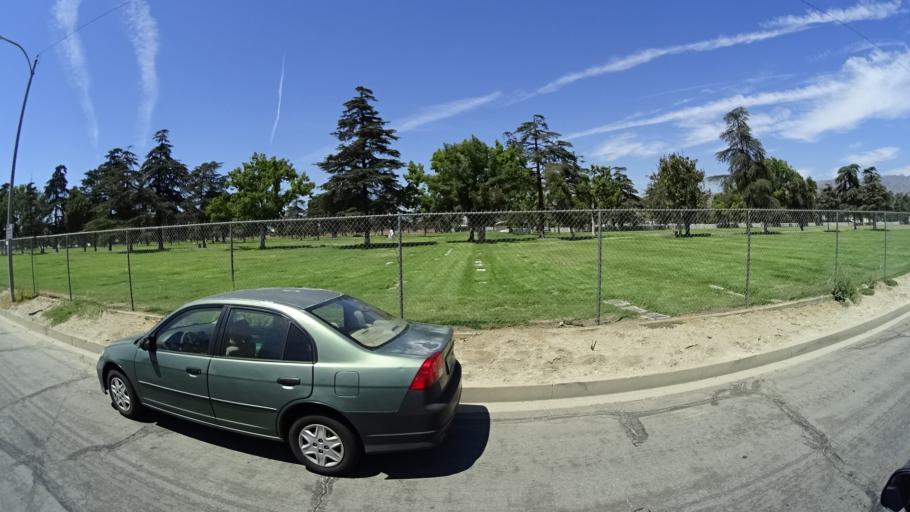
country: US
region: California
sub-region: Los Angeles County
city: North Hollywood
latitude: 34.1884
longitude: -118.3572
